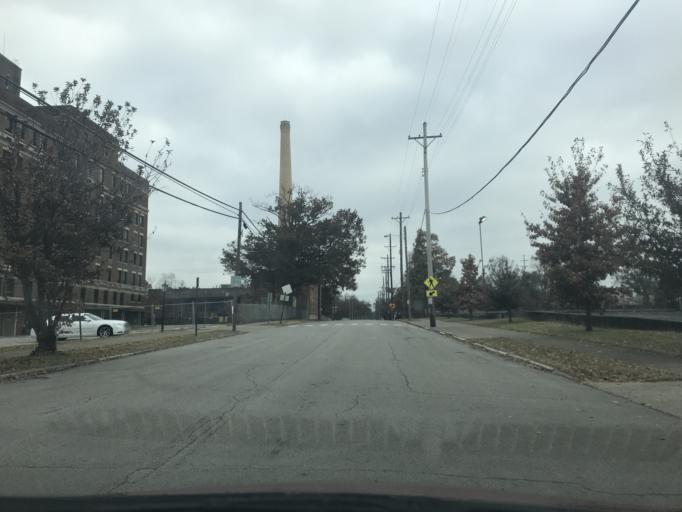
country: US
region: Kentucky
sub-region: Jefferson County
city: Louisville
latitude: 38.2409
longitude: -85.7340
